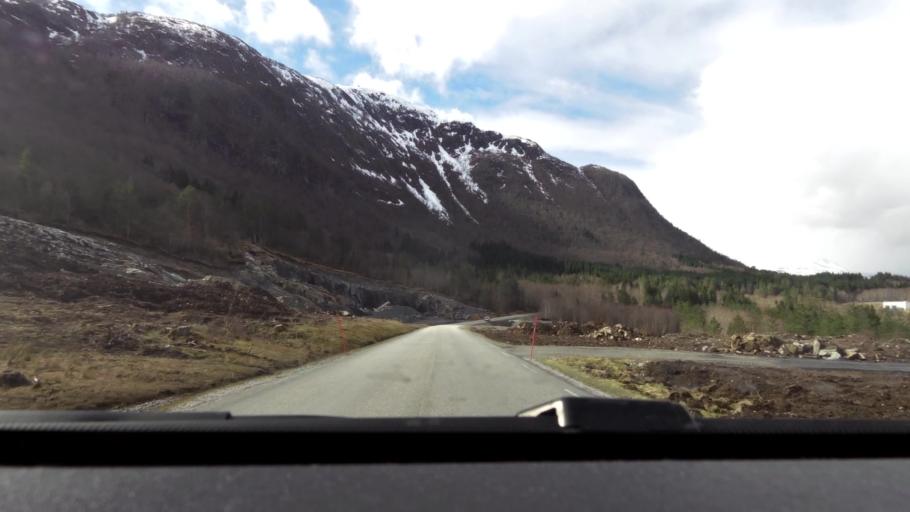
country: NO
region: More og Romsdal
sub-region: Averoy
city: Bruhagen
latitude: 63.0981
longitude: 7.6281
